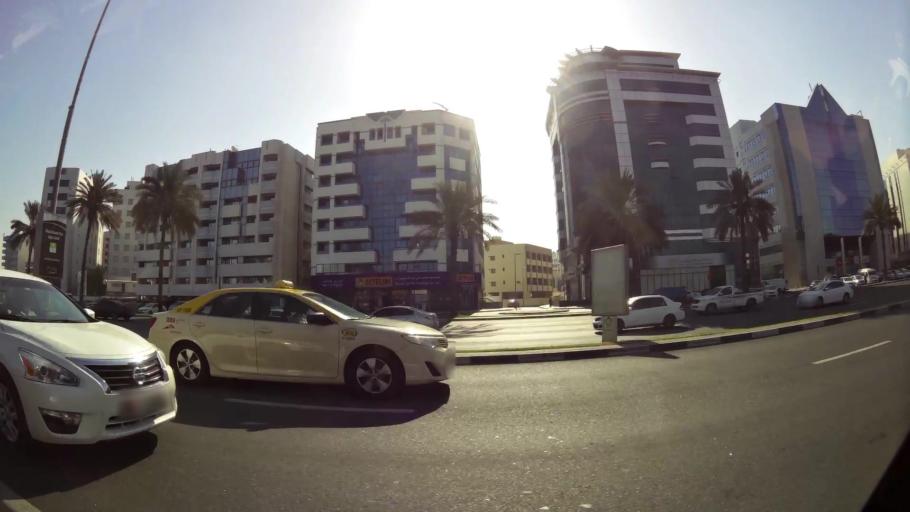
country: AE
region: Ash Shariqah
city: Sharjah
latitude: 25.2589
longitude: 55.2845
